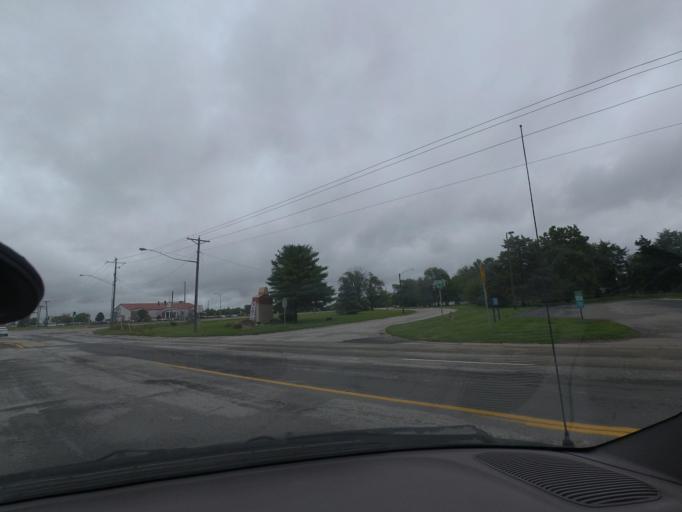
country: US
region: Illinois
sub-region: Macon County
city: Harristown
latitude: 39.8460
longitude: -89.0289
